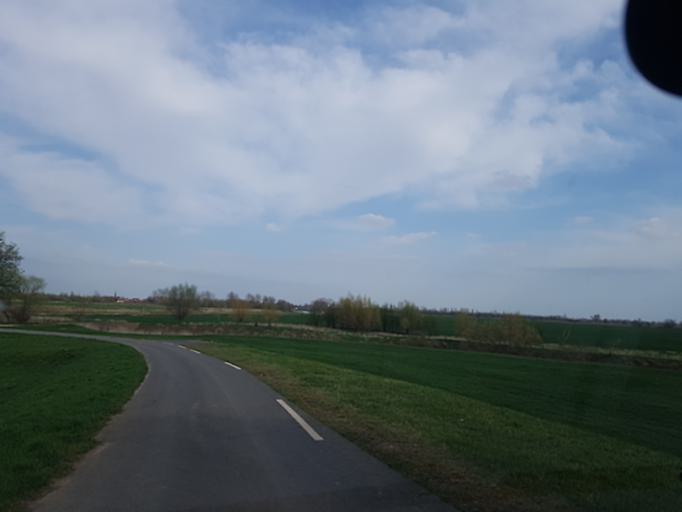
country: DE
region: Brandenburg
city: Muhlberg
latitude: 51.4356
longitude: 13.1899
